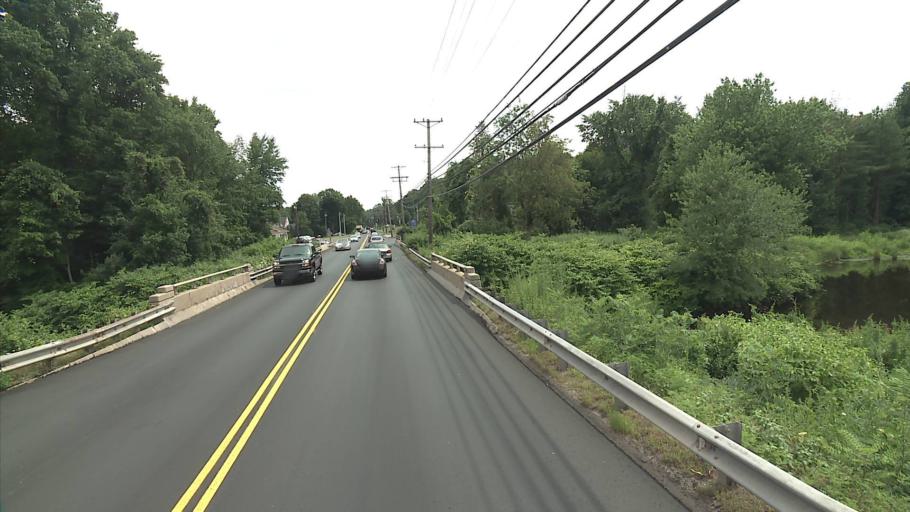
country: US
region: Connecticut
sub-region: New Haven County
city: Seymour
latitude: 41.4060
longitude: -73.0931
